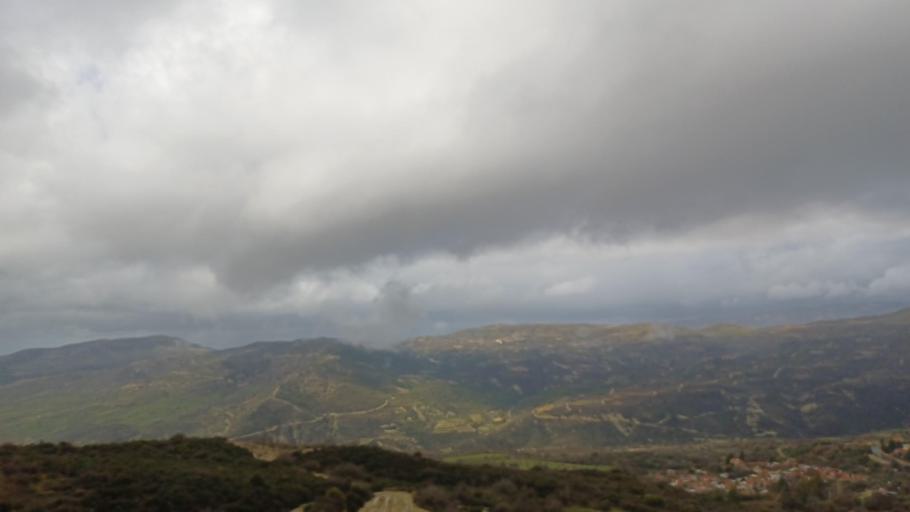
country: CY
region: Limassol
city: Pachna
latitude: 34.8328
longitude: 32.7438
